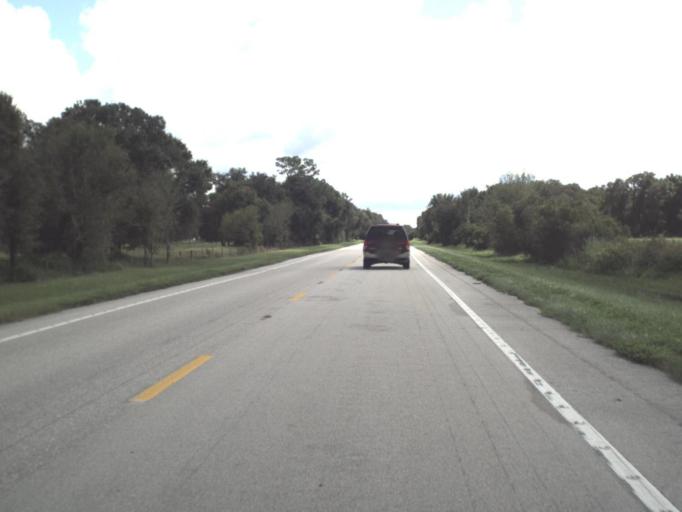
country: US
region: Florida
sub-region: DeSoto County
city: Arcadia
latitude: 27.2779
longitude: -82.0222
